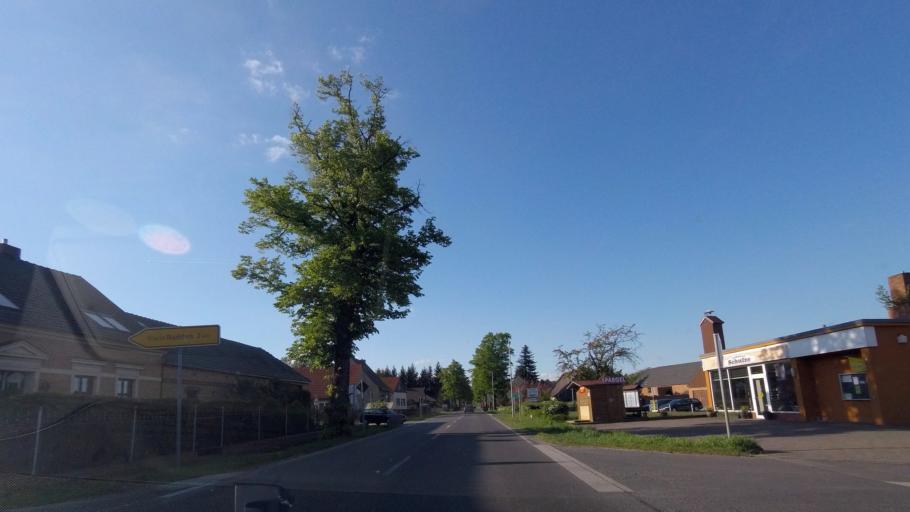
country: DE
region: Brandenburg
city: Luebben
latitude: 51.8871
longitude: 13.9016
